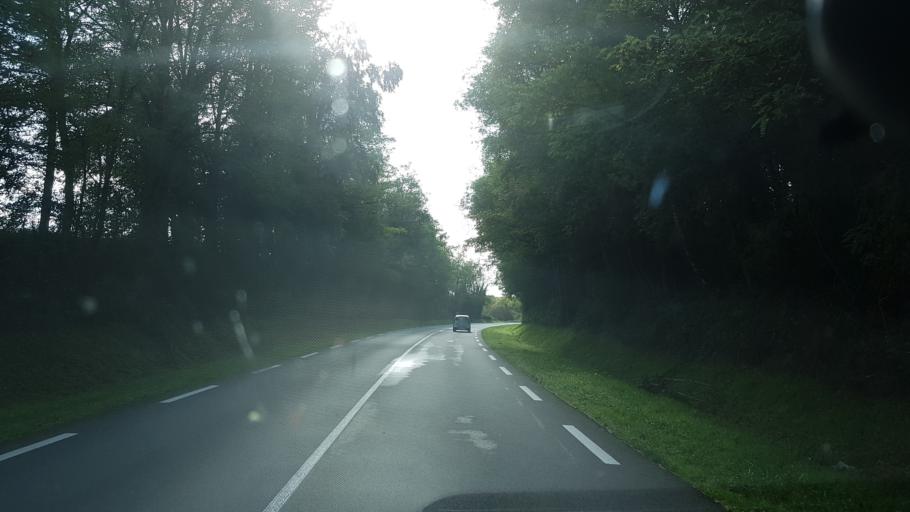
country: FR
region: Poitou-Charentes
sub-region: Departement de la Charente
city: Confolens
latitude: 45.9929
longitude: 0.6279
